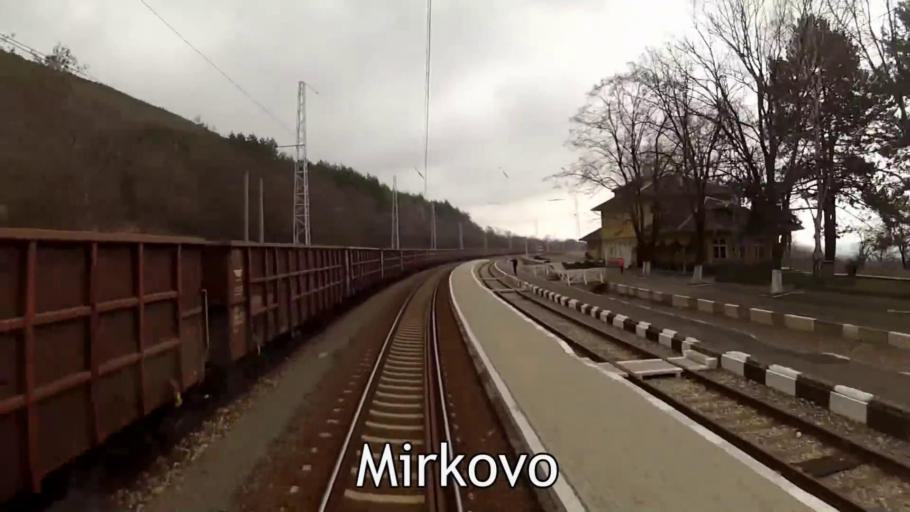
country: BG
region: Sofiya
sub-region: Obshtina Mirkovo
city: Mirkovo
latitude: 42.7002
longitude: 24.0076
